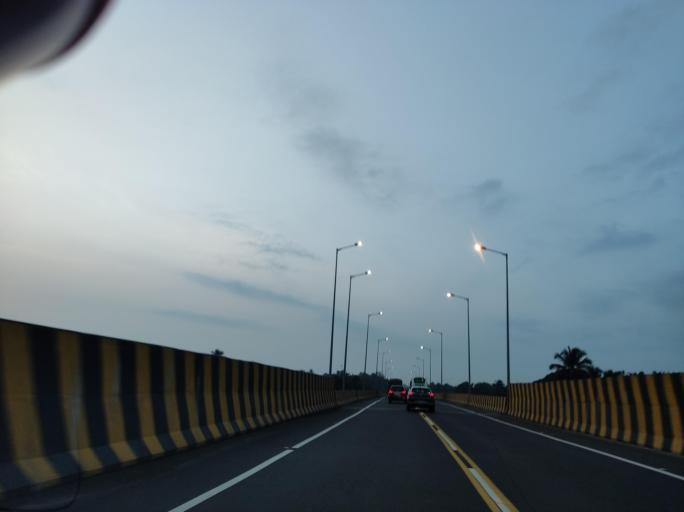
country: IN
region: Kerala
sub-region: Alappuzha
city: Alleppey
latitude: 9.4769
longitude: 76.3239
